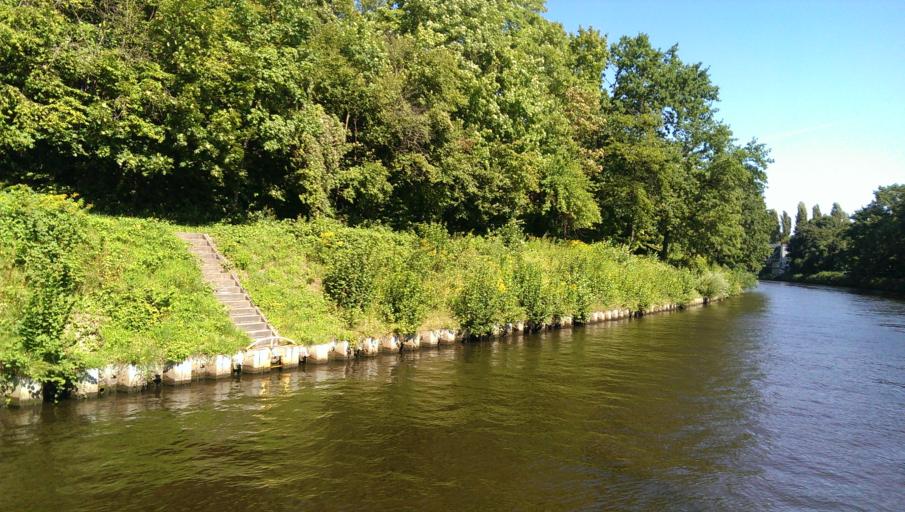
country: DE
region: Berlin
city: Lankwitz
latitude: 52.4429
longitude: 13.3593
